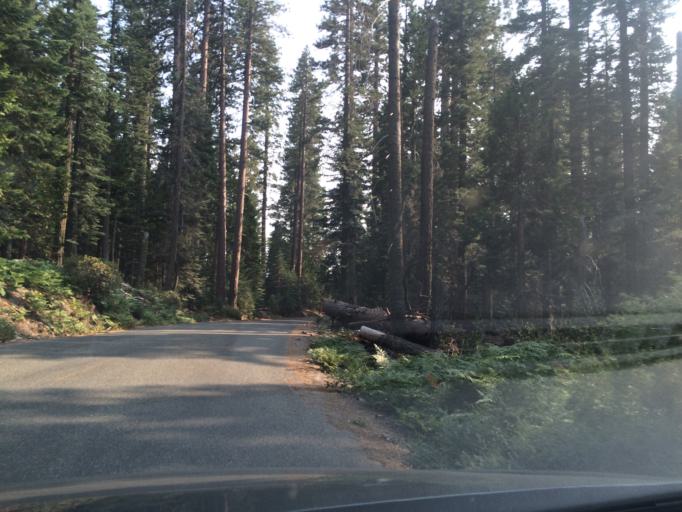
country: US
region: California
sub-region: Sierra County
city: Downieville
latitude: 39.3652
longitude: -120.6722
